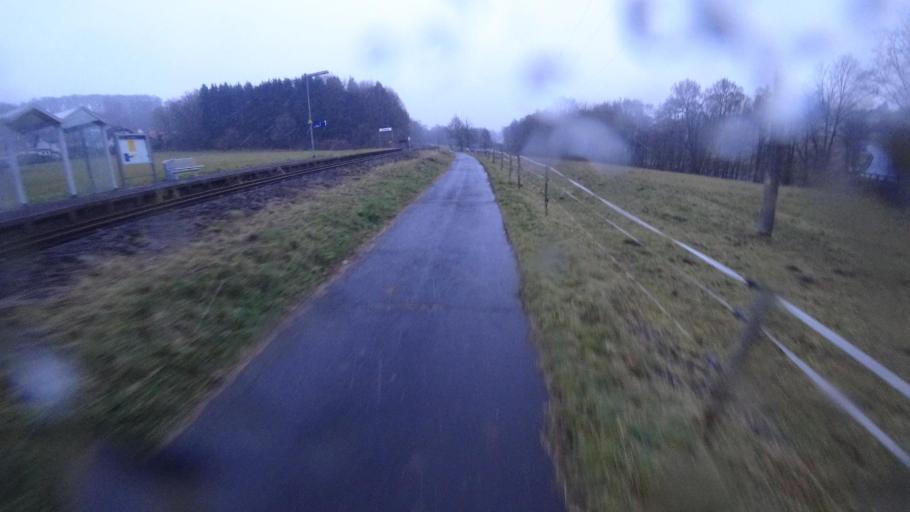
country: DE
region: Rheinland-Pfalz
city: Enspel
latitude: 50.6152
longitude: 7.8829
